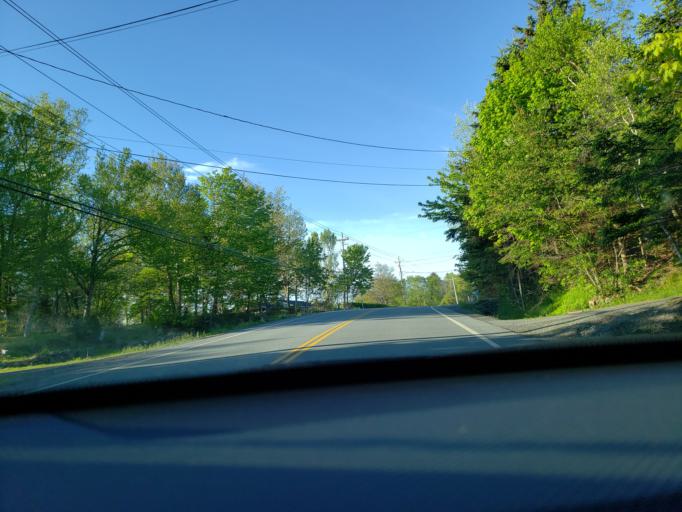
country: CA
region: Nova Scotia
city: Cole Harbour
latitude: 44.7317
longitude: -63.3932
